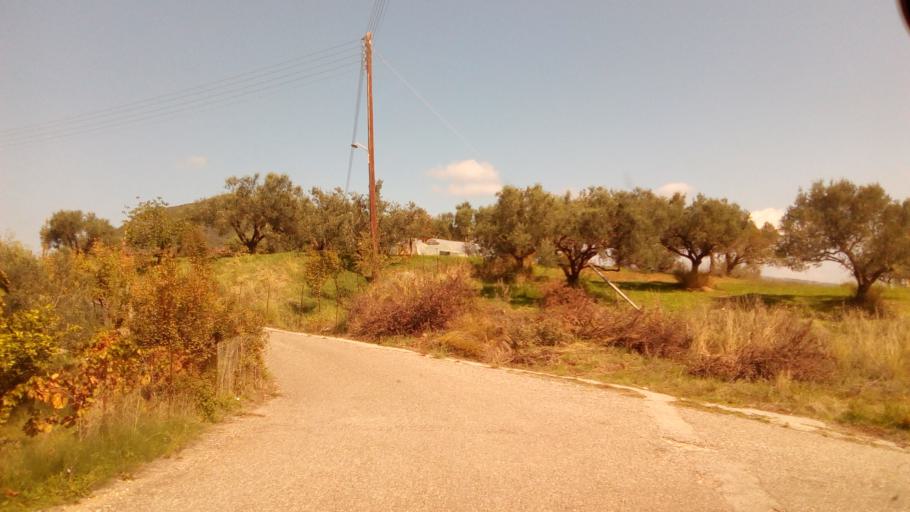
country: GR
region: West Greece
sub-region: Nomos Aitolias kai Akarnanias
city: Antirrio
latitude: 38.3680
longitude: 21.7741
